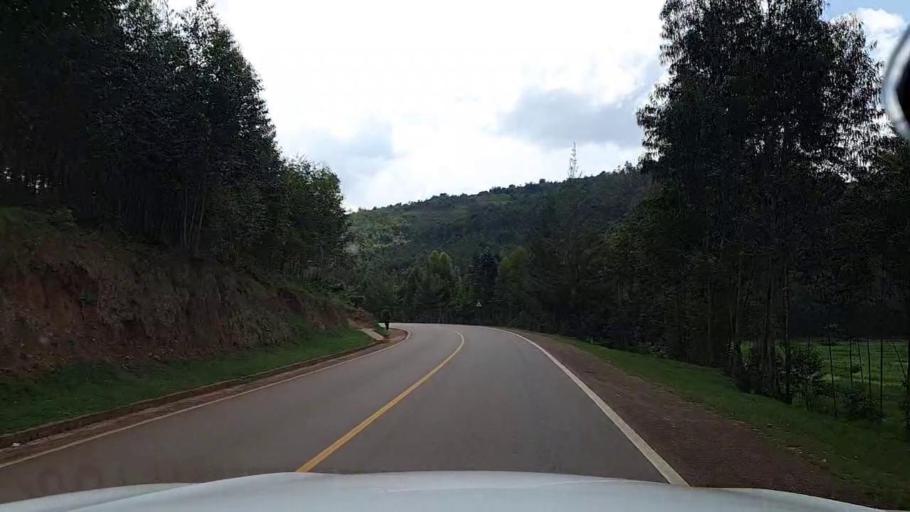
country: RW
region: Kigali
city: Kigali
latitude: -1.8191
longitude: 30.1126
